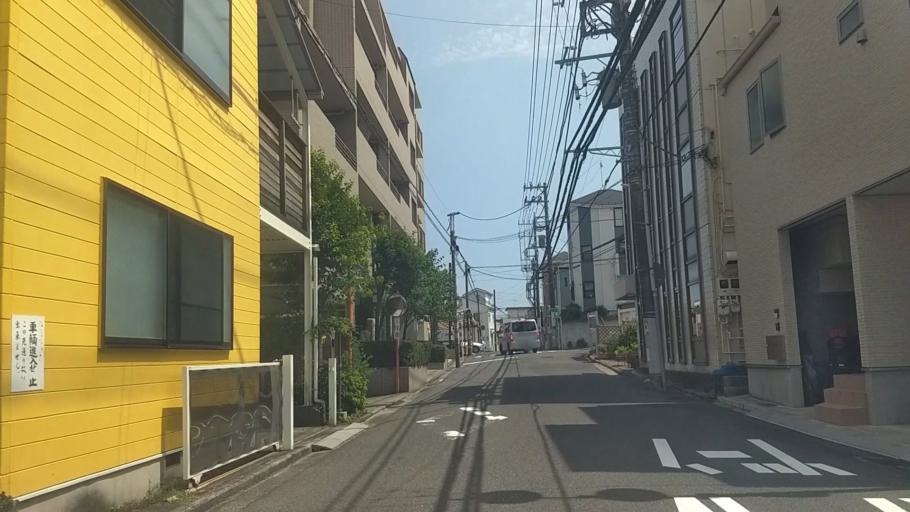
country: JP
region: Kanagawa
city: Yokohama
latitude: 35.4904
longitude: 139.6353
